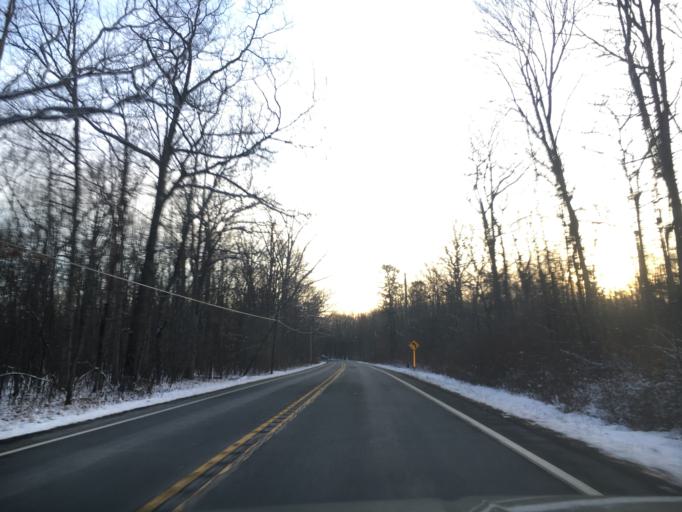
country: US
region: Pennsylvania
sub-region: Pike County
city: Hemlock Farms
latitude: 41.2254
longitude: -75.0792
